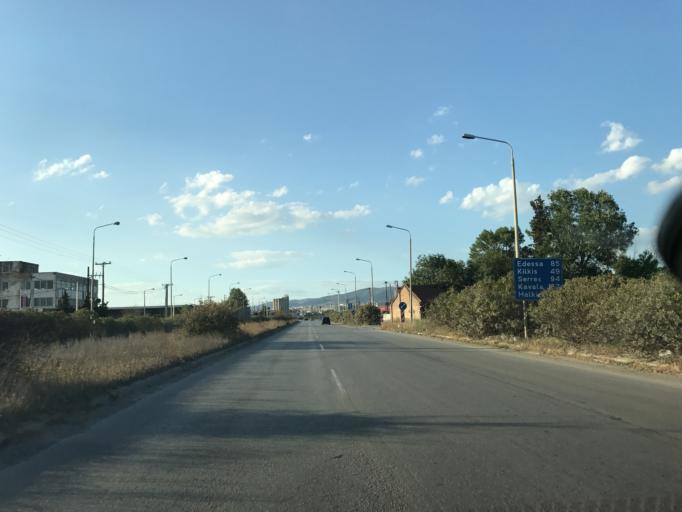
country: GR
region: Central Macedonia
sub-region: Nomos Thessalonikis
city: Menemeni
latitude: 40.6605
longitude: 22.8818
